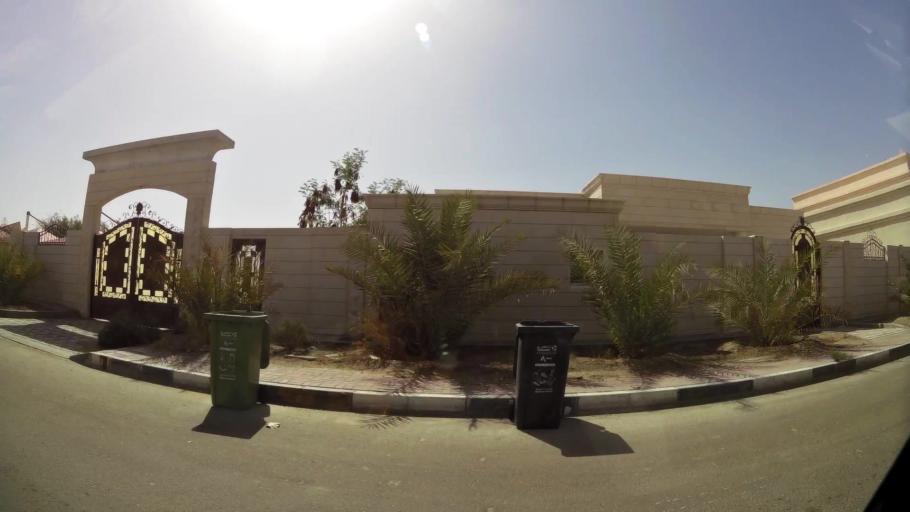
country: OM
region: Al Buraimi
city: Al Buraymi
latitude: 24.3063
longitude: 55.7986
